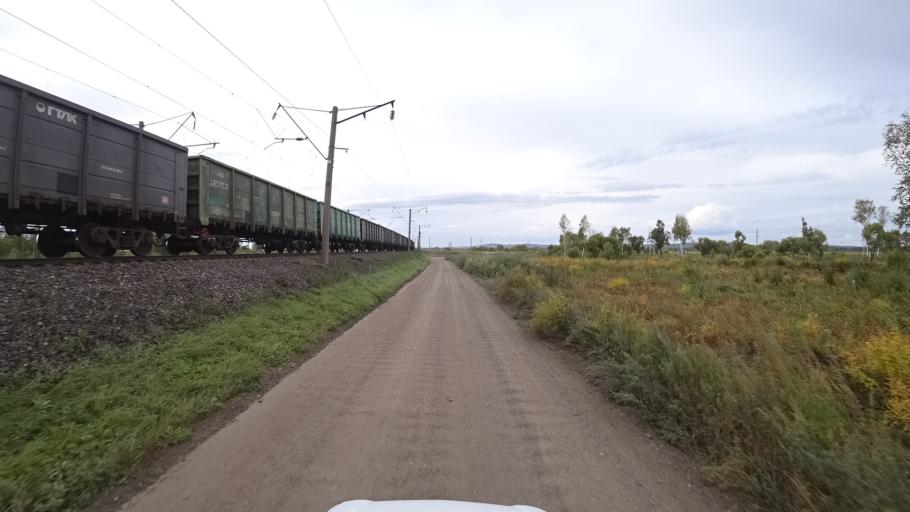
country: RU
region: Amur
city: Arkhara
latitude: 49.3692
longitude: 130.1420
